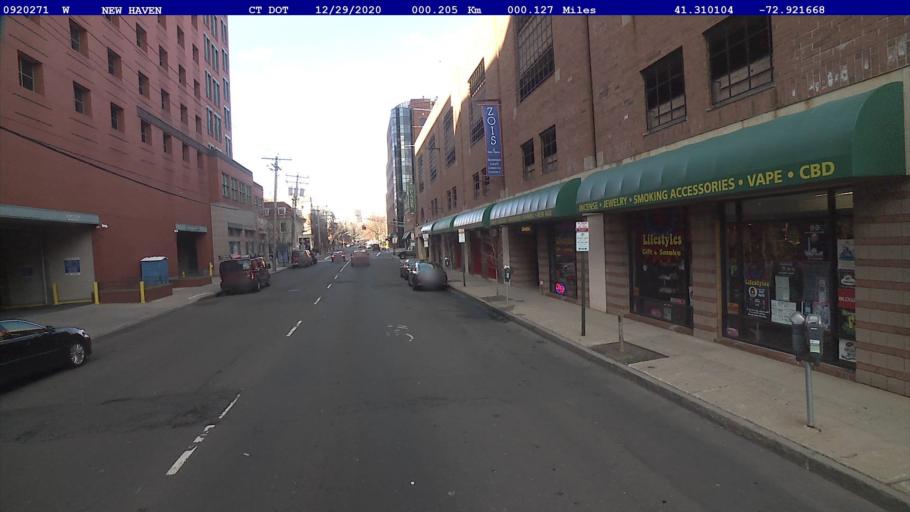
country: US
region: Connecticut
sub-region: New Haven County
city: New Haven
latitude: 41.3101
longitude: -72.9217
